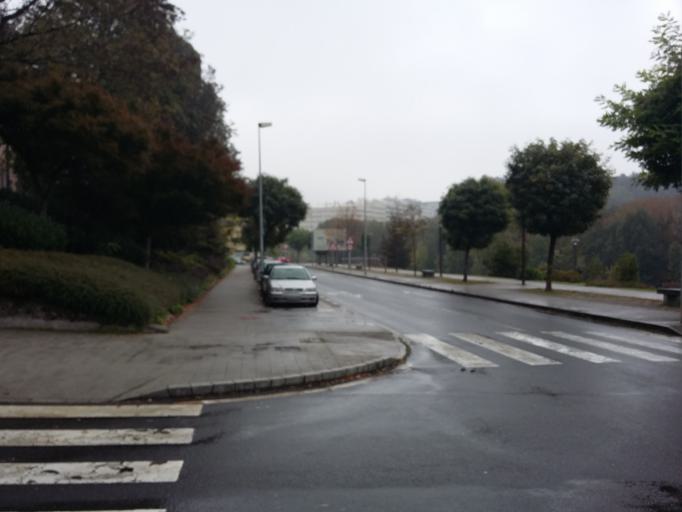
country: ES
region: Galicia
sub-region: Provincia da Coruna
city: Santiago de Compostela
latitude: 42.8674
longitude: -8.5481
